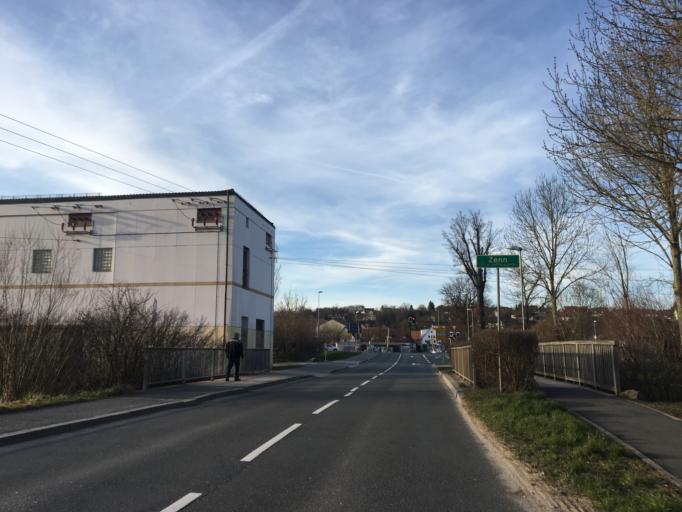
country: DE
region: Bavaria
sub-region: Regierungsbezirk Mittelfranken
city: Wilhermsdorf
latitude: 49.4792
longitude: 10.7180
